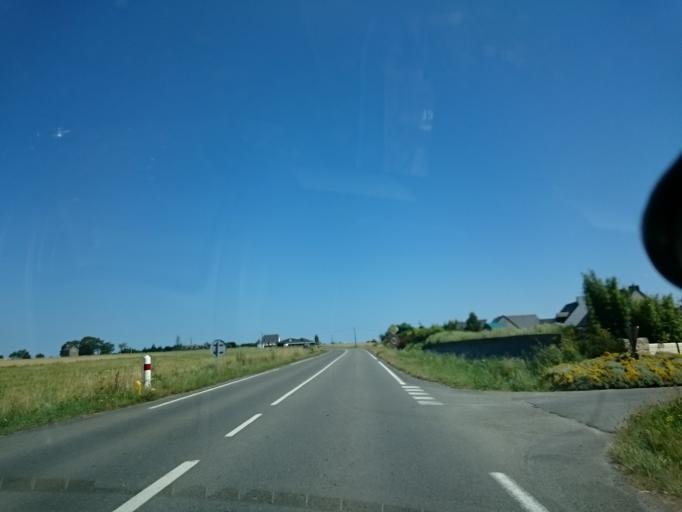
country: FR
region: Brittany
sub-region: Departement d'Ille-et-Vilaine
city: La Gouesniere
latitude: 48.6066
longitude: -1.9007
